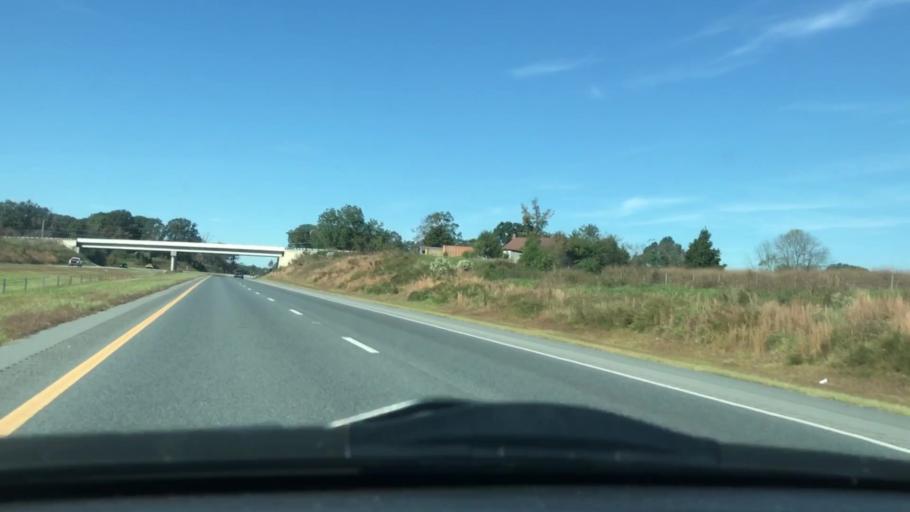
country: US
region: North Carolina
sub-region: Randolph County
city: Randleman
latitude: 35.8544
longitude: -79.8794
